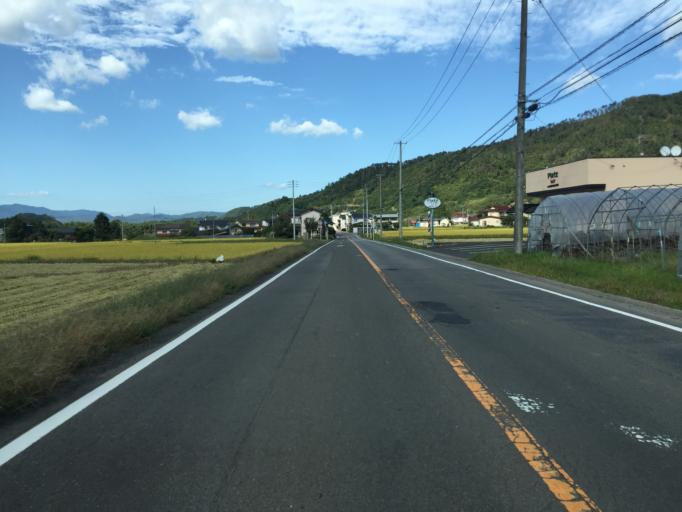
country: JP
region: Fukushima
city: Yanagawamachi-saiwaicho
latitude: 37.8125
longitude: 140.6188
